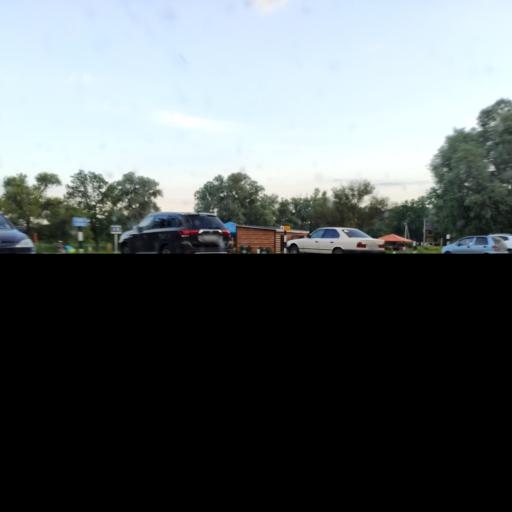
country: RU
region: Voronezj
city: Ramon'
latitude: 51.9488
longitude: 39.3811
